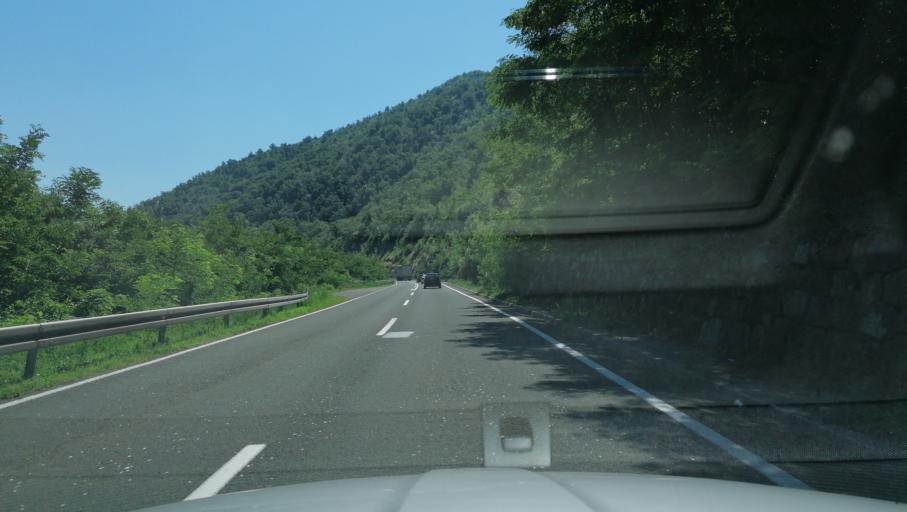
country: RS
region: Central Serbia
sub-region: Raski Okrug
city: Kraljevo
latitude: 43.5927
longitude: 20.5709
